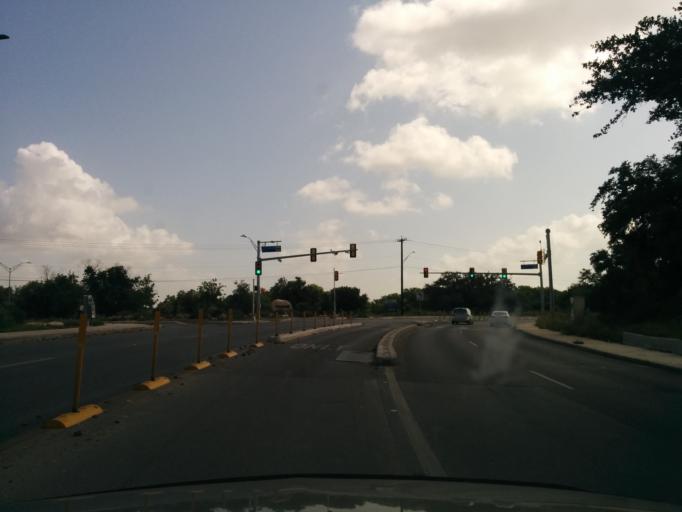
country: US
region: Texas
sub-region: Bexar County
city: Shavano Park
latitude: 29.5621
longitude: -98.6148
